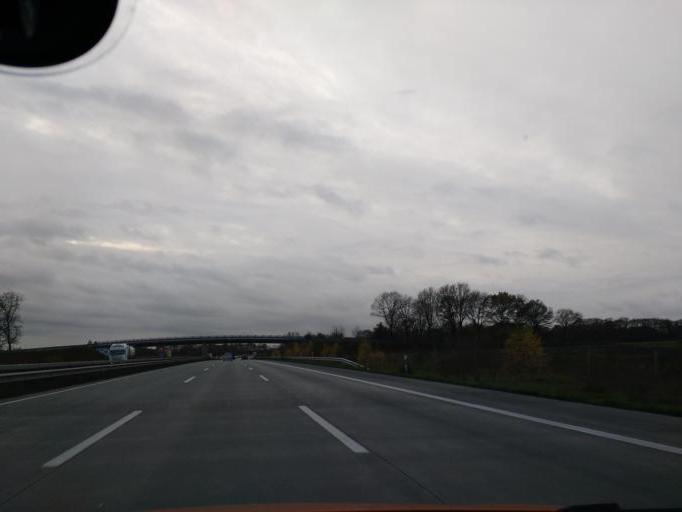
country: DE
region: Lower Saxony
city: Elsdorf
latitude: 53.2444
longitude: 9.4057
